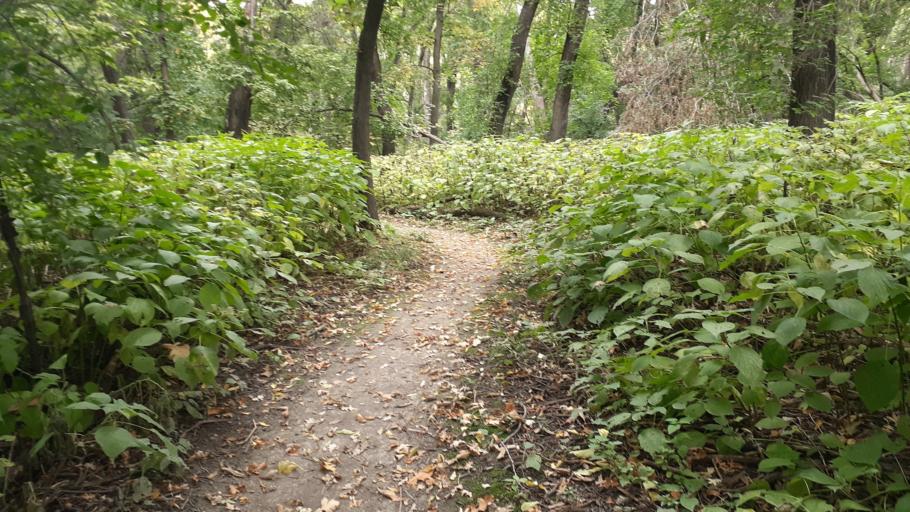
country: US
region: Minnesota
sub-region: Clay County
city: Oakport
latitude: 46.9108
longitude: -96.7613
